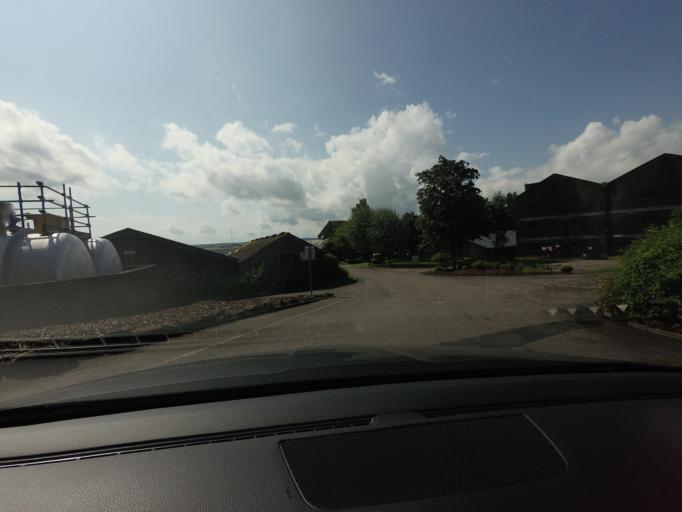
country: GB
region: Scotland
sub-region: Highland
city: Alness
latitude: 57.6886
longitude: -4.2402
